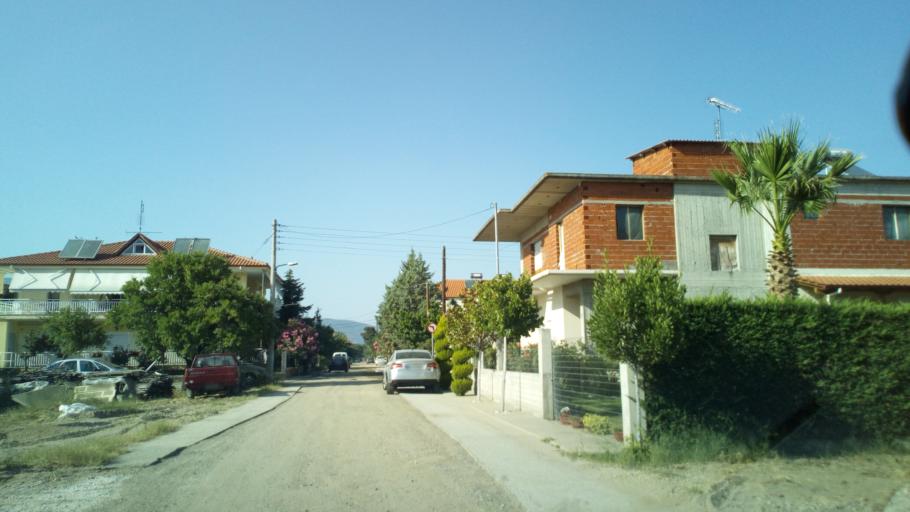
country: GR
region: Central Macedonia
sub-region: Nomos Thessalonikis
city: Nea Vrasna
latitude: 40.7038
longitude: 23.6990
